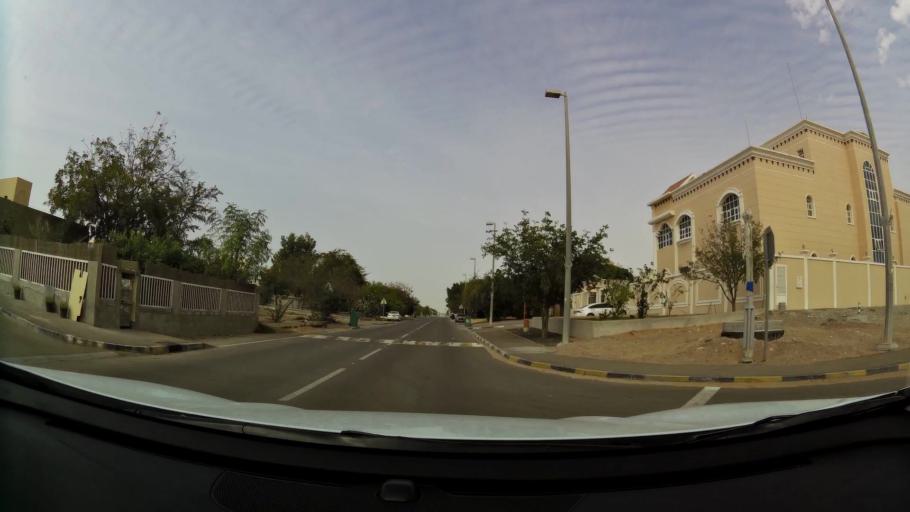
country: AE
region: Abu Dhabi
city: Abu Dhabi
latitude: 24.5549
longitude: 54.6881
